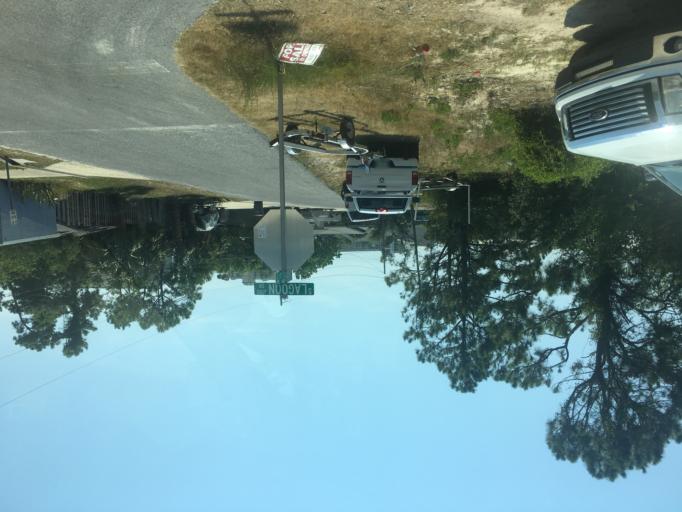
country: US
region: Florida
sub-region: Bay County
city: Lower Grand Lagoon
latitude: 30.1566
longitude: -85.7675
